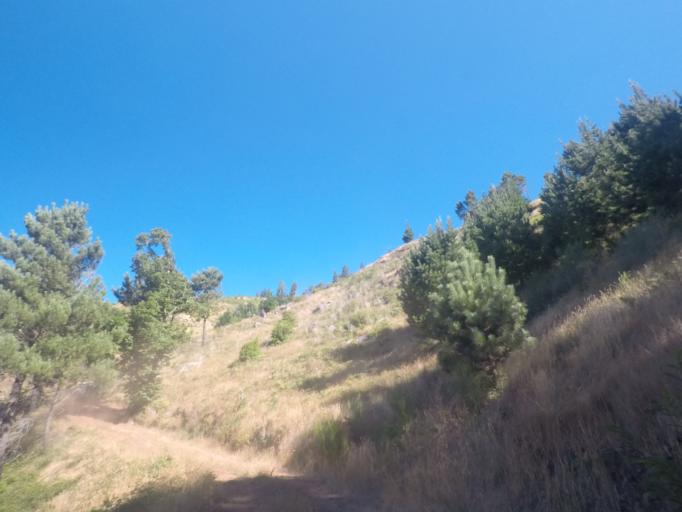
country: PT
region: Madeira
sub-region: Funchal
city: Nossa Senhora do Monte
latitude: 32.7047
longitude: -16.9085
